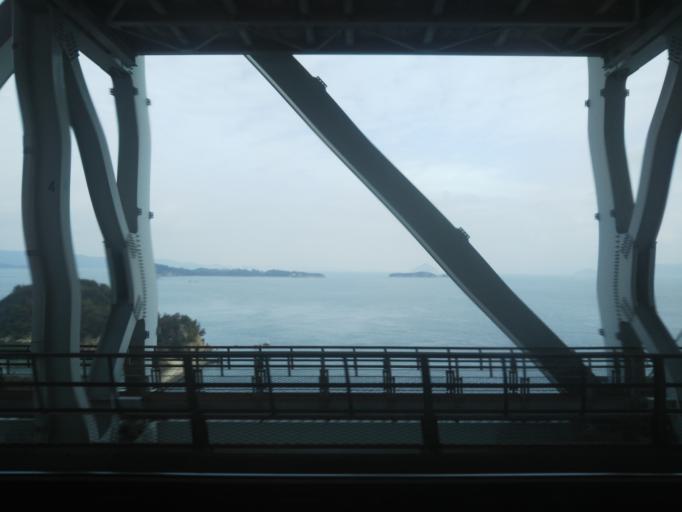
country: JP
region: Kagawa
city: Sakaidecho
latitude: 34.4124
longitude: 133.8061
